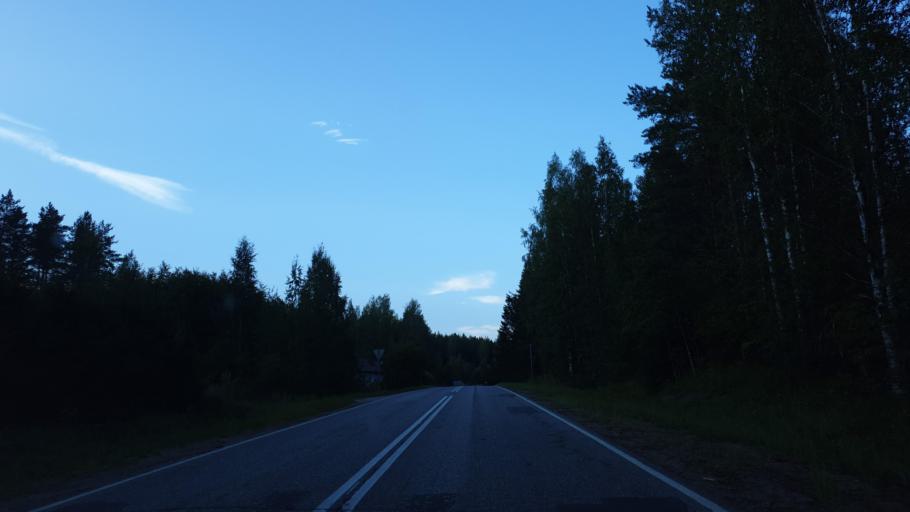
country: FI
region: Northern Savo
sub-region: Koillis-Savo
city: Kaavi
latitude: 62.9248
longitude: 28.6917
